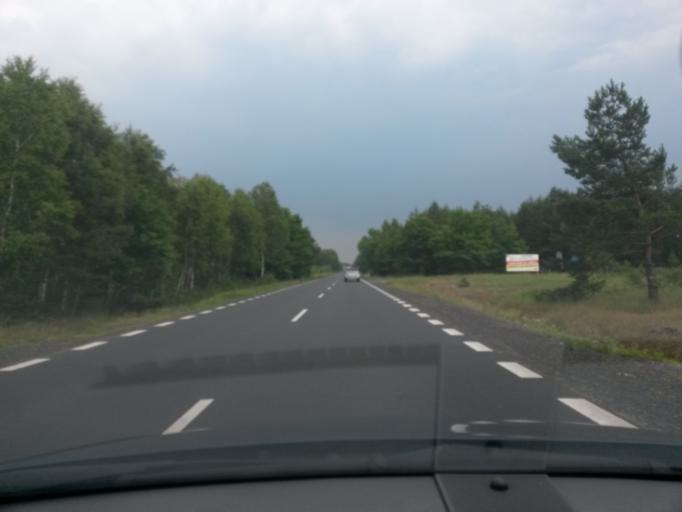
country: PL
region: Silesian Voivodeship
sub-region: Powiat czestochowski
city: Olsztyn
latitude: 50.7601
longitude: 19.2125
